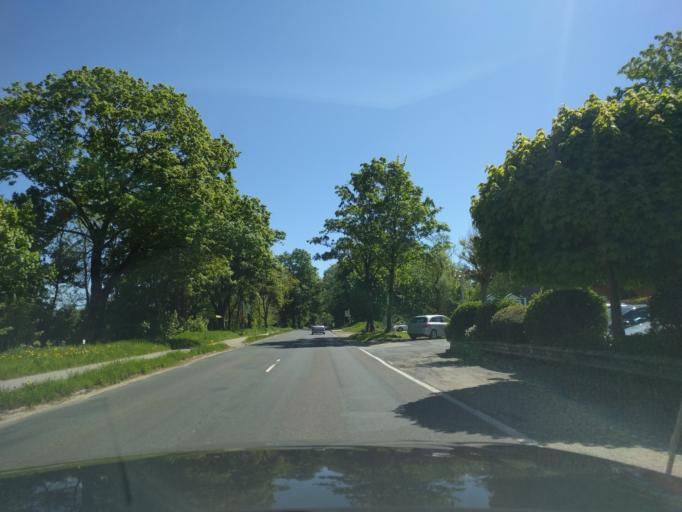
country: DE
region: Lower Saxony
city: Seevetal
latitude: 53.3948
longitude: 10.0122
